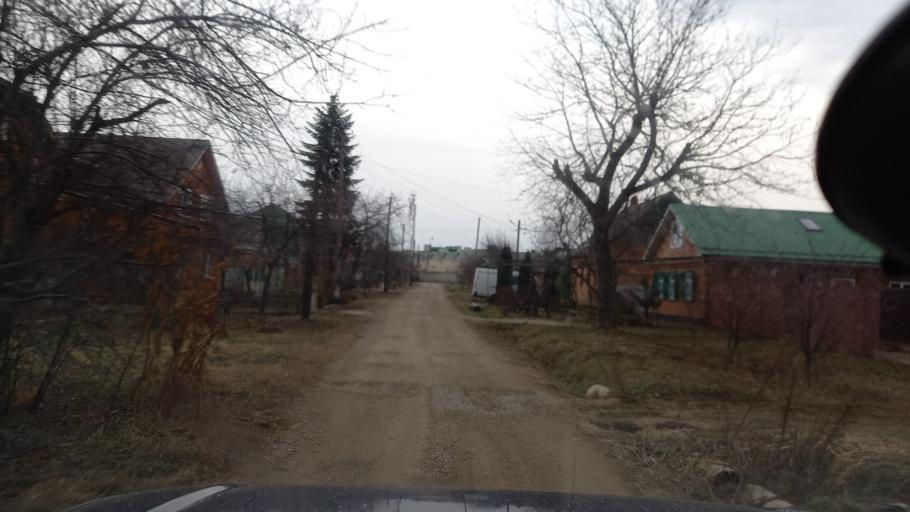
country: RU
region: Adygeya
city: Maykop
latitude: 44.5923
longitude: 40.1000
